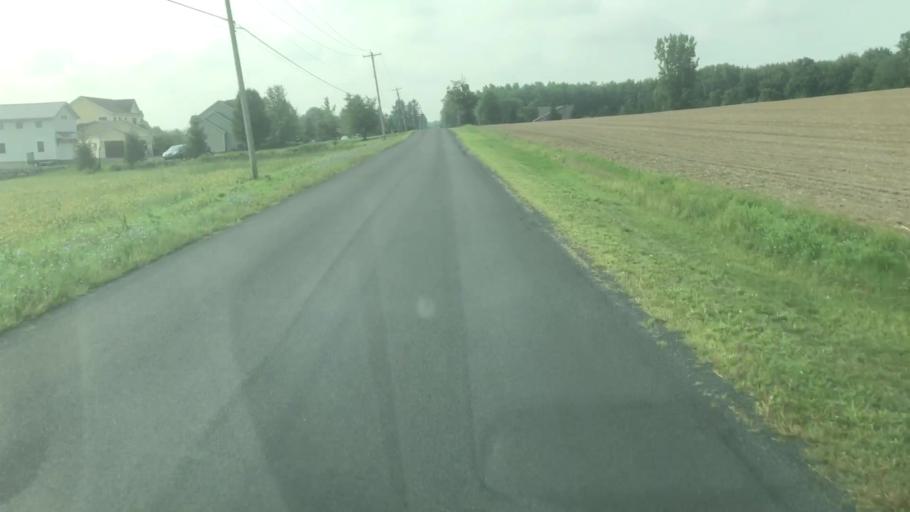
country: US
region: New York
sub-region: Onondaga County
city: Skaneateles
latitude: 42.9252
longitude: -76.4571
